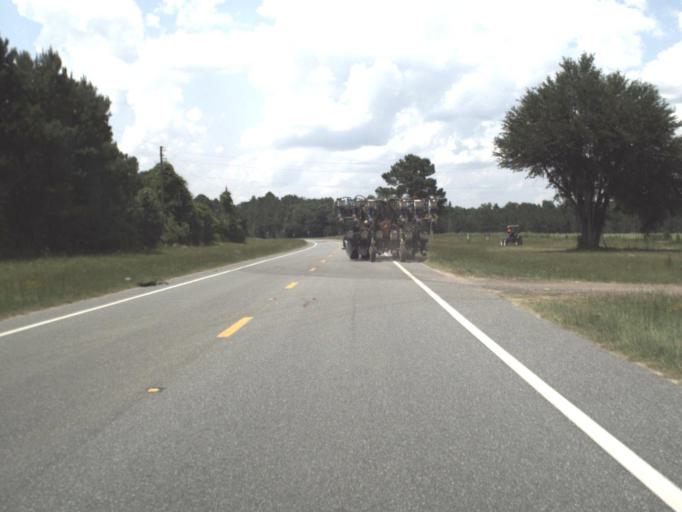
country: US
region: Georgia
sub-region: Echols County
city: Statenville
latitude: 30.5914
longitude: -83.0934
